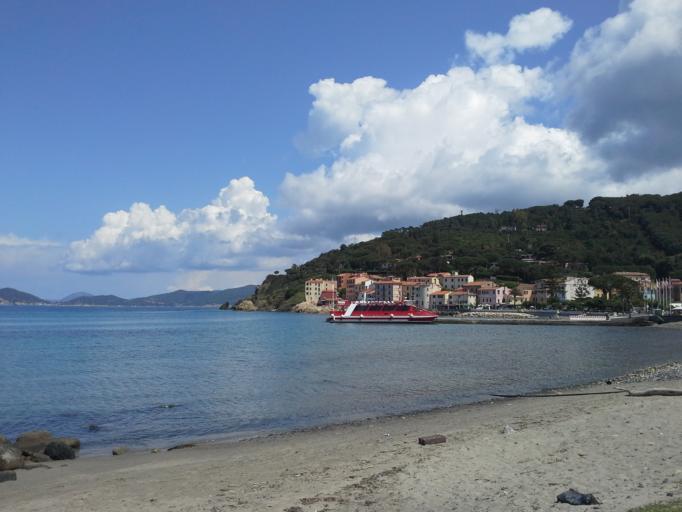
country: IT
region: Tuscany
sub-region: Provincia di Livorno
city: Marciana Marina
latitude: 42.8066
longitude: 10.1968
